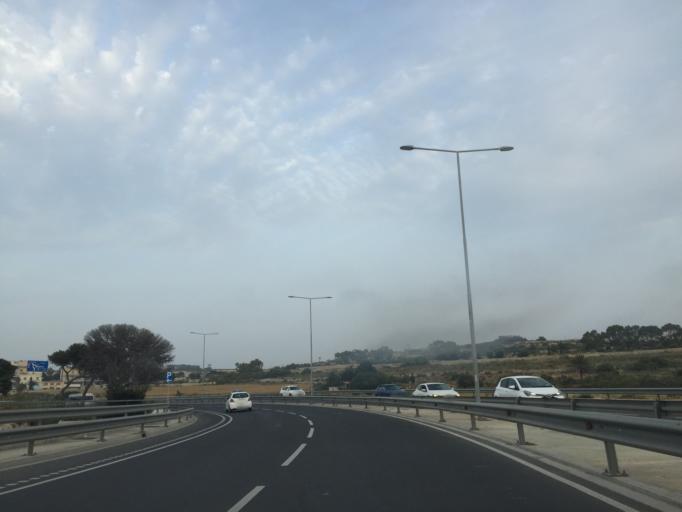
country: MT
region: Saint Paul's Bay
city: San Pawl il-Bahar
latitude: 35.9430
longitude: 14.4197
